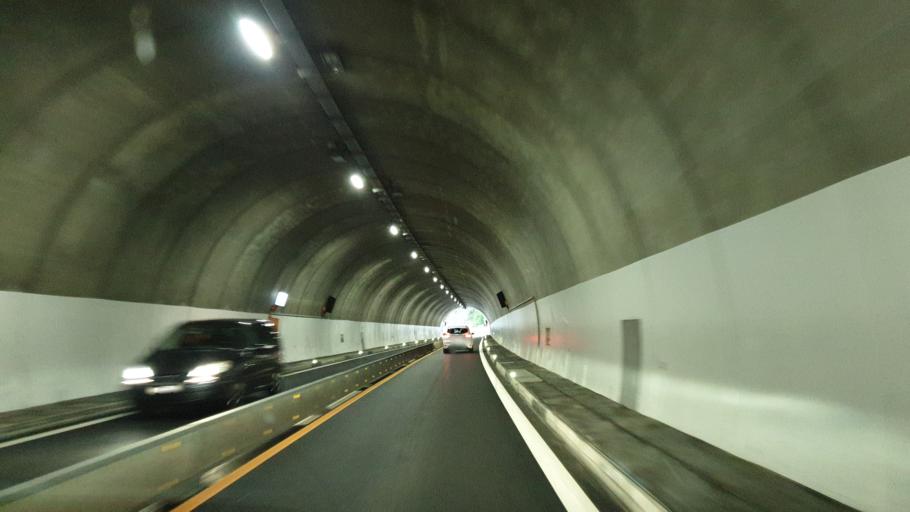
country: CH
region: Schwyz
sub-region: Bezirk Schwyz
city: Arth
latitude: 47.0529
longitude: 8.5250
